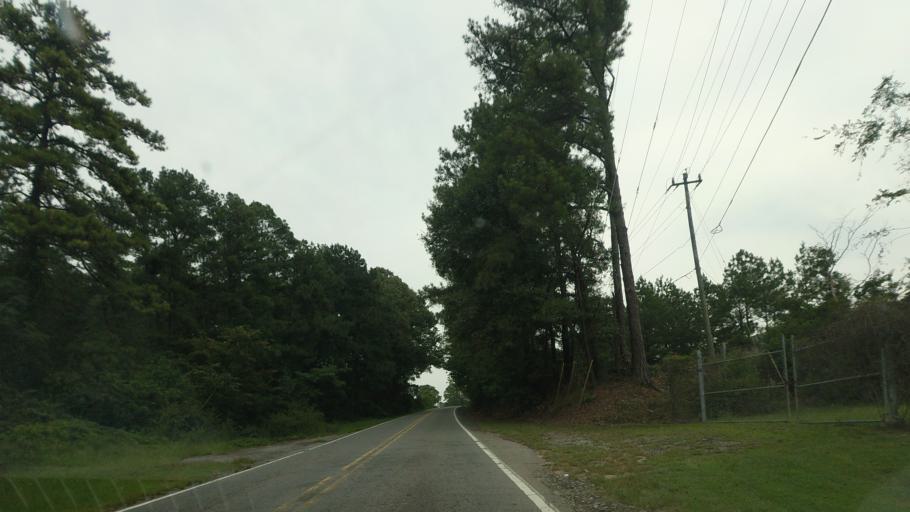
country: US
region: Georgia
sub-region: Houston County
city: Robins Air Force Base
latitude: 32.5898
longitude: -83.5949
